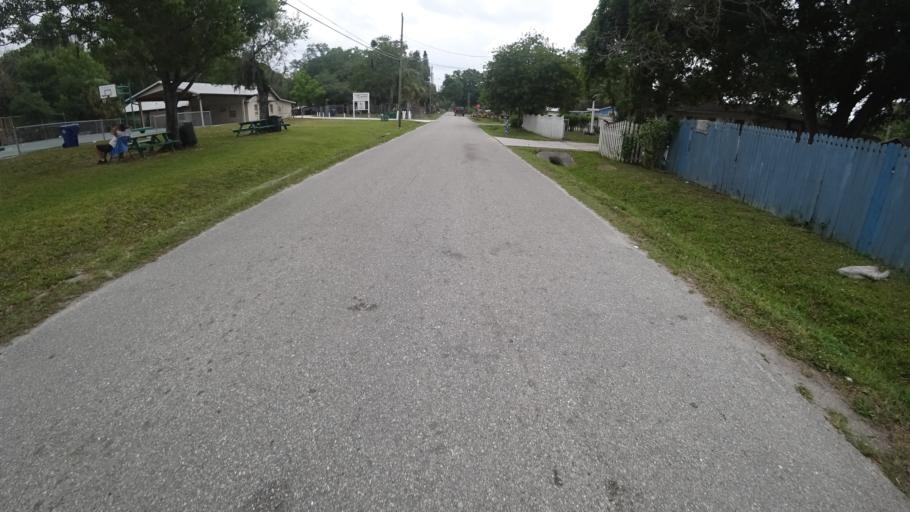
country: US
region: Florida
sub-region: Manatee County
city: Samoset
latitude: 27.4714
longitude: -82.5450
